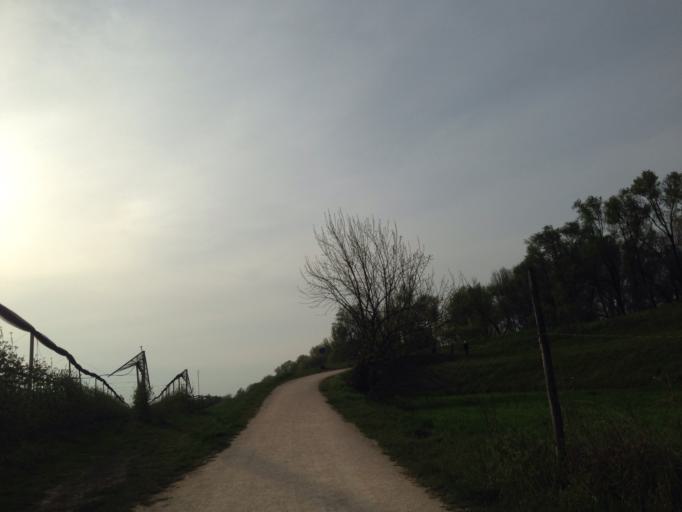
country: IT
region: Veneto
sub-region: Provincia di Verona
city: Zevio
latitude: 45.3769
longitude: 11.1187
